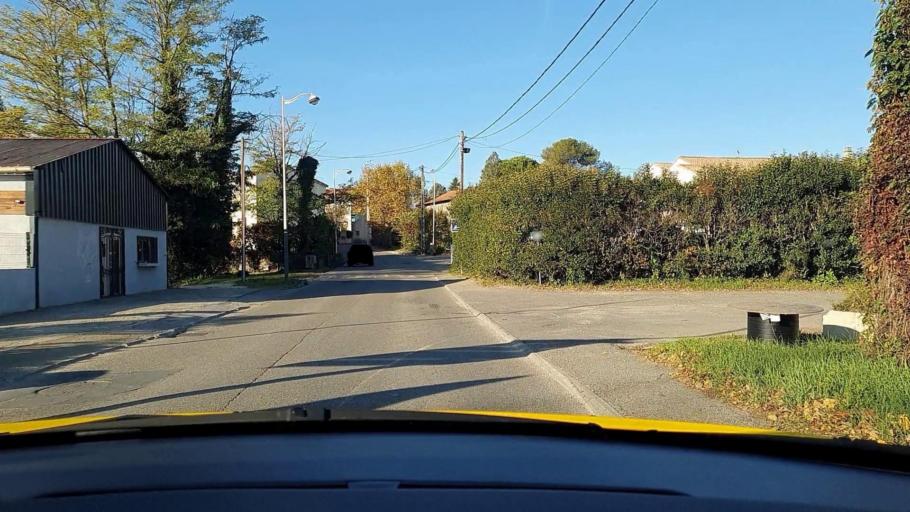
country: FR
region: Languedoc-Roussillon
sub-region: Departement du Gard
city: Salindres
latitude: 44.1778
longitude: 4.1524
